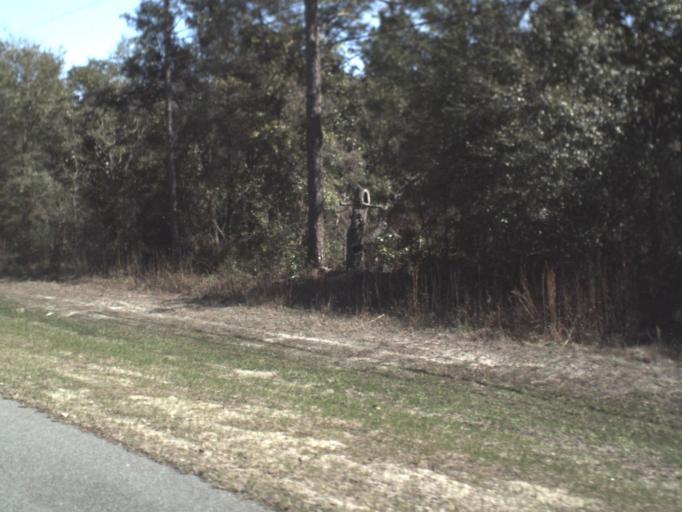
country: US
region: Florida
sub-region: Bay County
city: Laguna Beach
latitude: 30.3155
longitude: -85.8089
